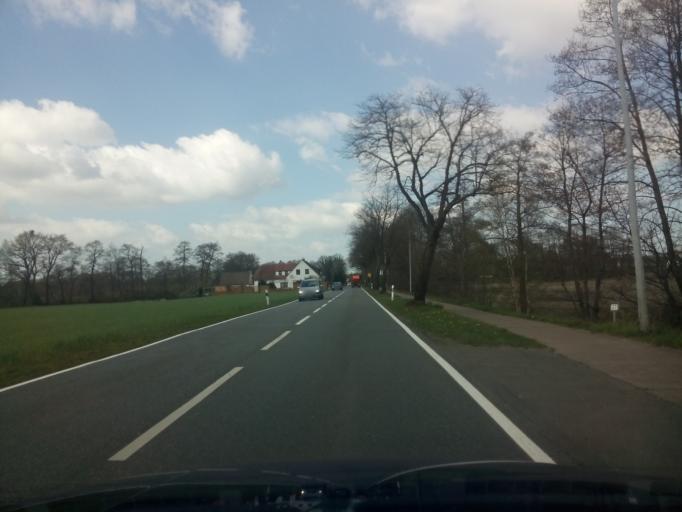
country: DE
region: Lower Saxony
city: Lilienthal
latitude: 53.1657
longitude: 8.9276
